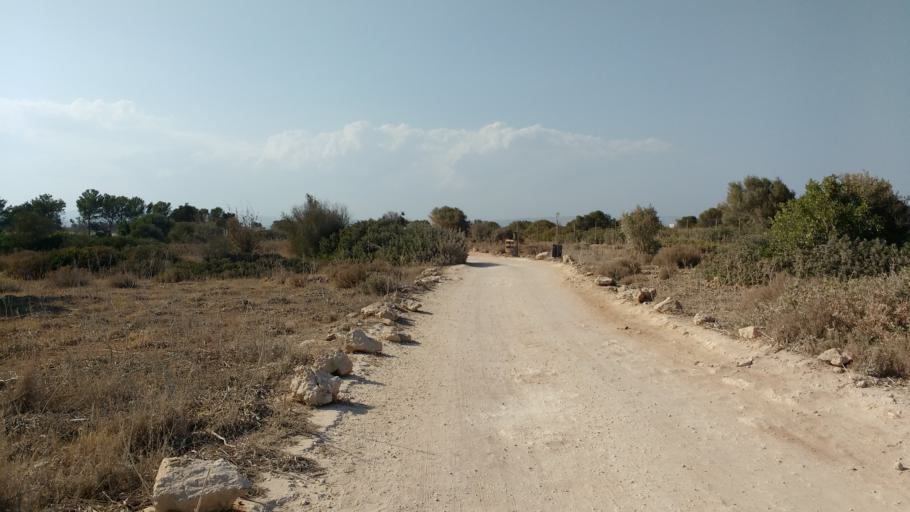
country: IT
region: Sicily
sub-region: Provincia di Siracusa
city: Noto
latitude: 36.8165
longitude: 15.0991
